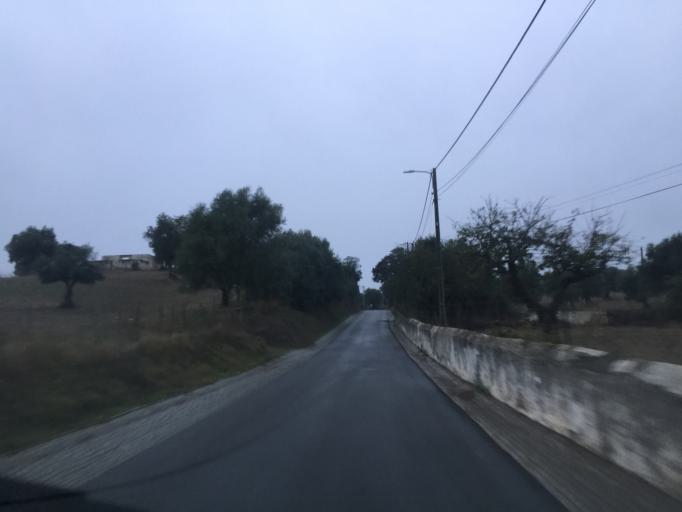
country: PT
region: Portalegre
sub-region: Avis
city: Avis
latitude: 39.0534
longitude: -7.8974
